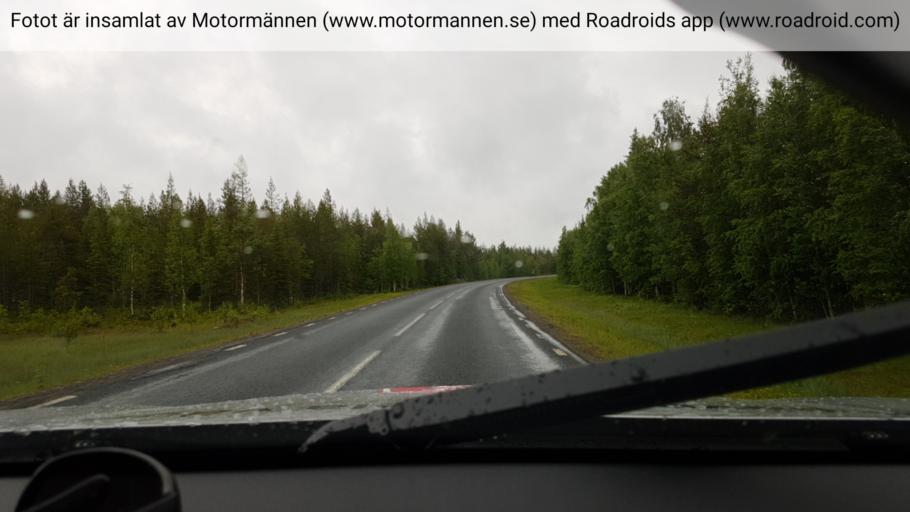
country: SE
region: Vaesterbotten
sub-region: Mala Kommun
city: Mala
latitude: 65.2454
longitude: 18.3087
